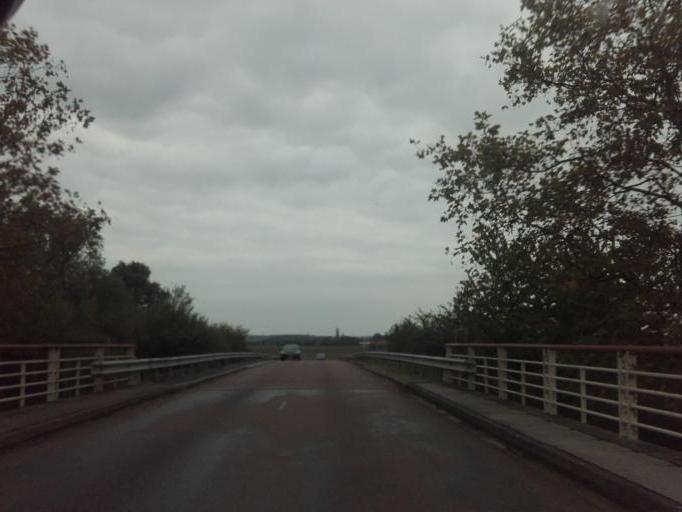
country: FR
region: Bourgogne
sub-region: Departement de la Cote-d'Or
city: Bligny-les-Beaune
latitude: 46.9890
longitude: 4.8528
